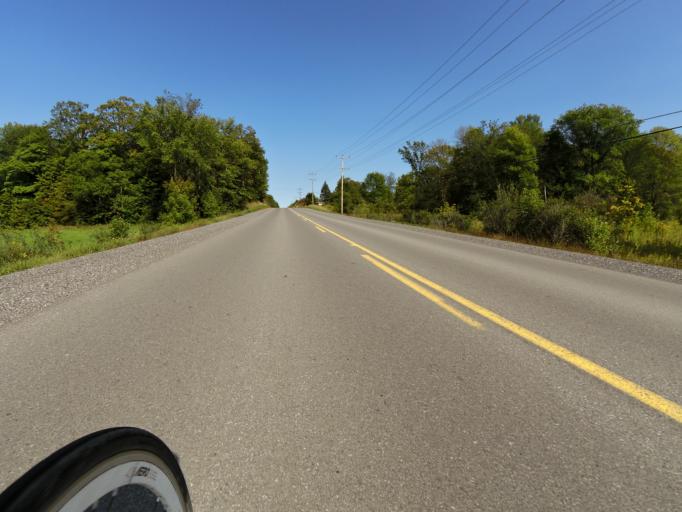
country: CA
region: Ontario
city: Arnprior
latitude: 45.4194
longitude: -76.1440
